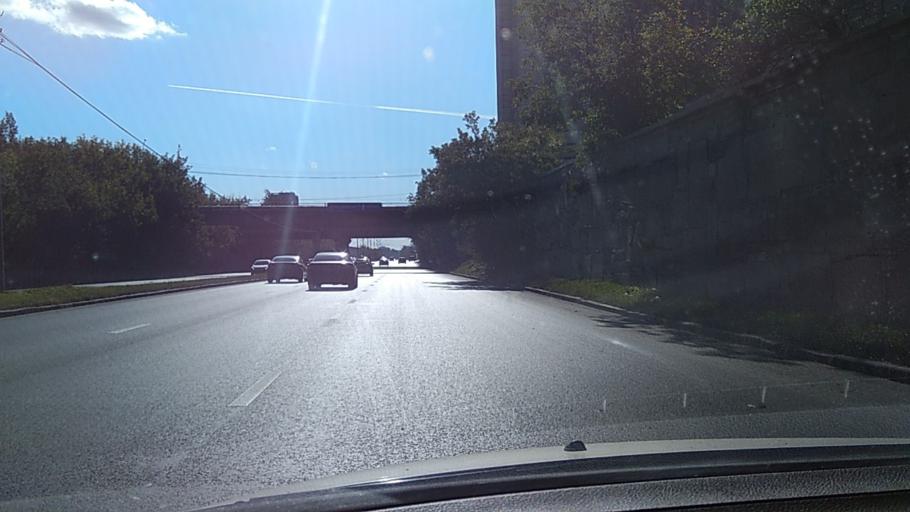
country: RU
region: Sverdlovsk
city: Sovkhoznyy
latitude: 56.8151
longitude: 60.5522
